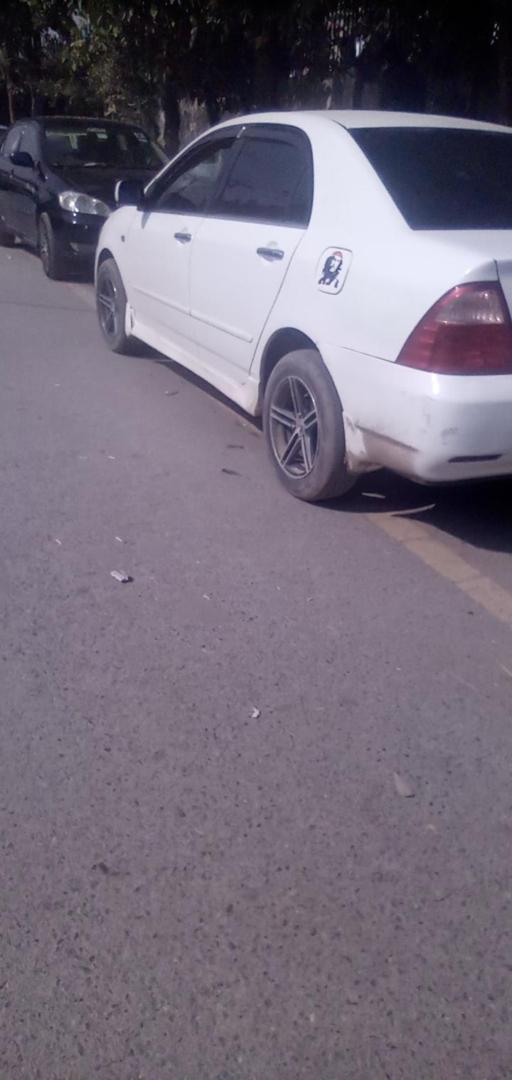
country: PK
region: Khyber Pakhtunkhwa
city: Peshawar
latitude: 33.9896
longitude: 71.4426
